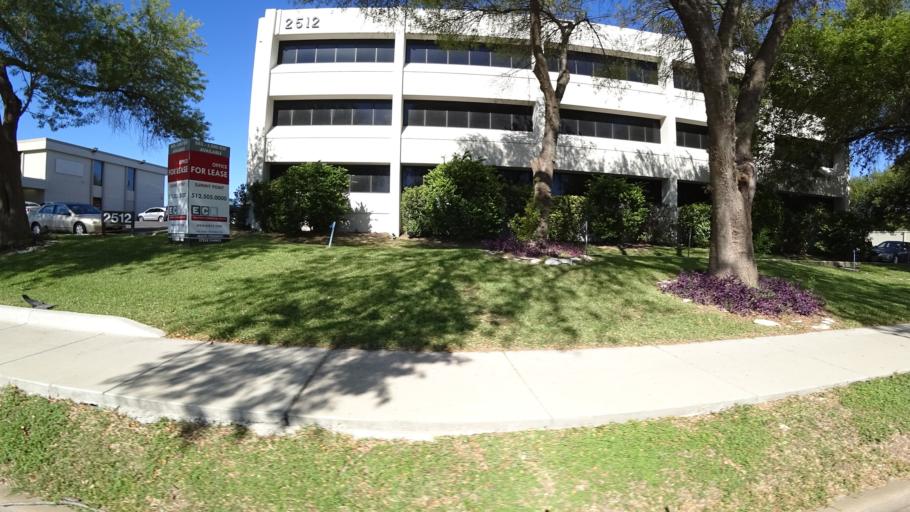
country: US
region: Texas
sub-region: Travis County
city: Austin
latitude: 30.2316
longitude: -97.7429
